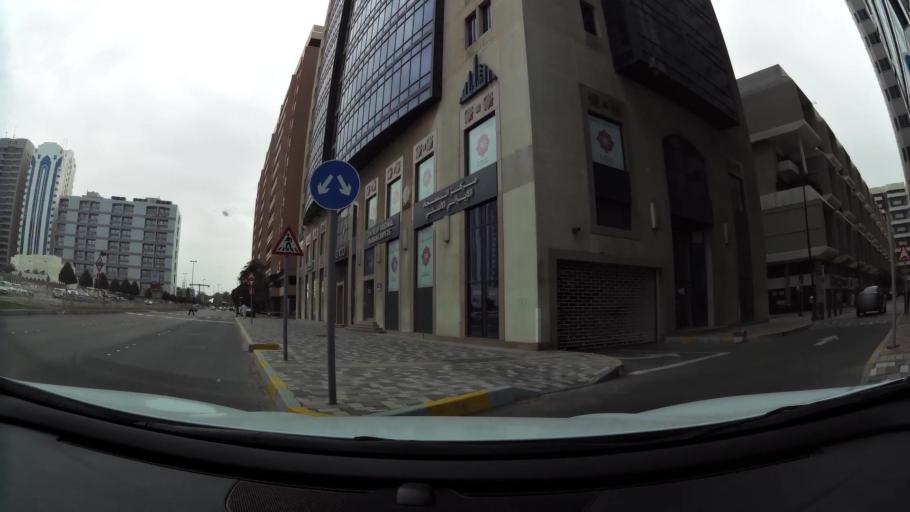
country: AE
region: Abu Dhabi
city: Abu Dhabi
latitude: 24.4719
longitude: 54.3417
